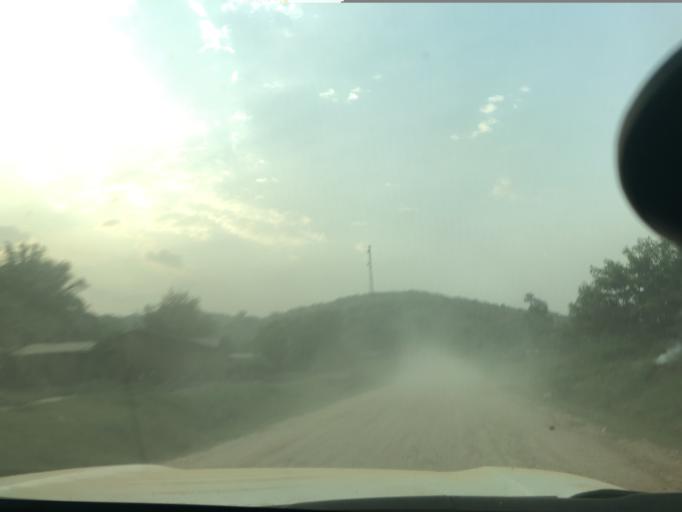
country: CD
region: Nord Kivu
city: Beni
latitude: 0.3698
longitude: 29.6166
